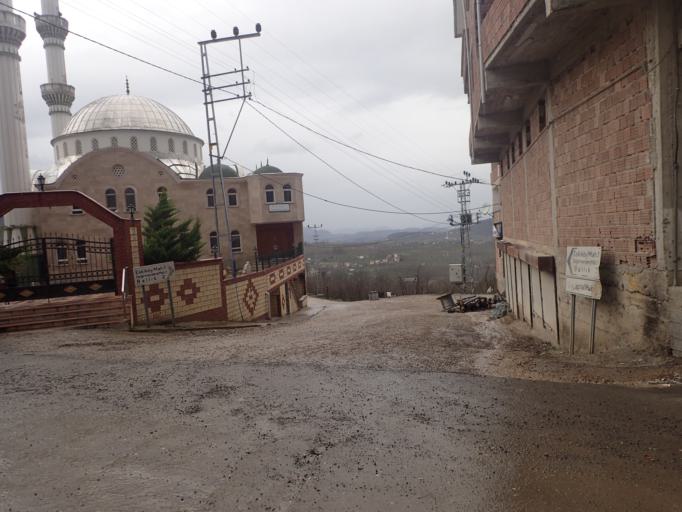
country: TR
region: Ordu
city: Kumru
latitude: 40.9433
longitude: 37.2617
